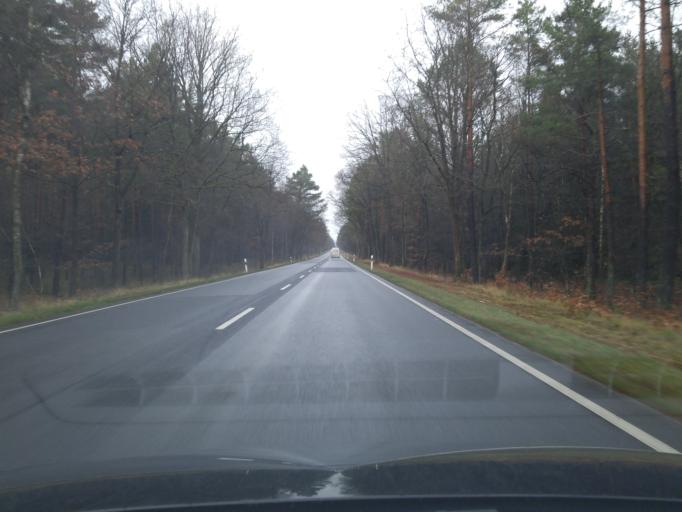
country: DE
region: Lower Saxony
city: Dedelstorf
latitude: 52.7177
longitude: 10.4814
